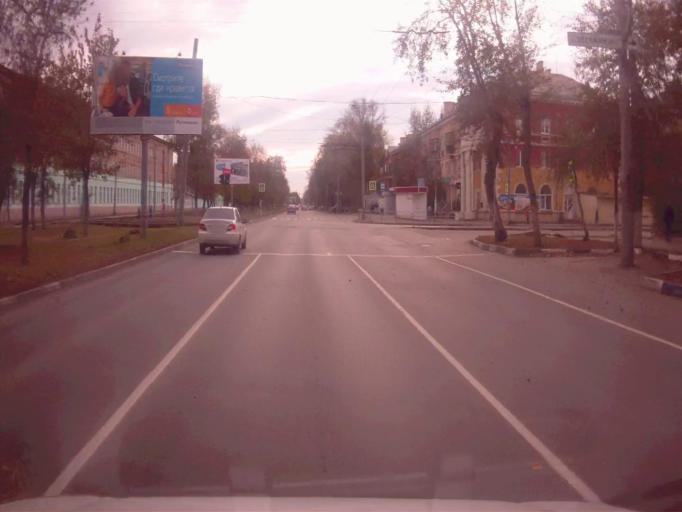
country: RU
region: Chelyabinsk
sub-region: Gorod Chelyabinsk
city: Chelyabinsk
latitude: 55.1215
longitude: 61.4729
